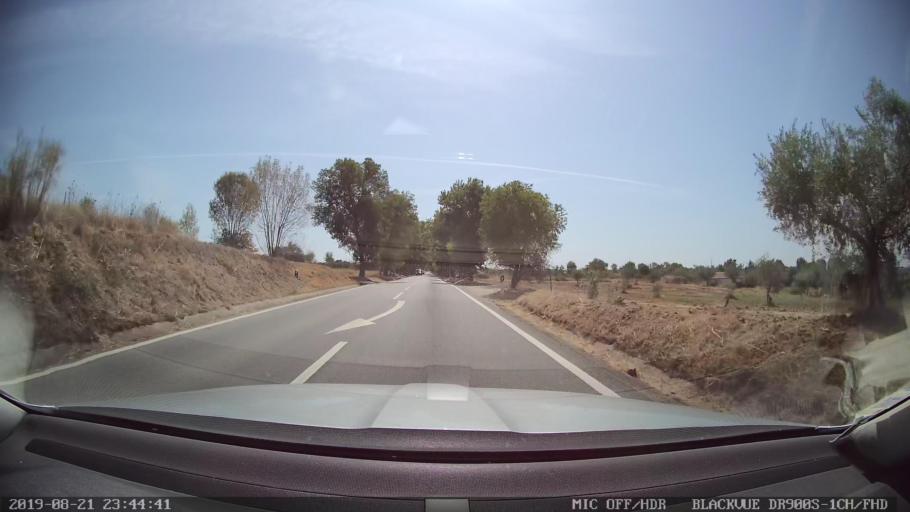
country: PT
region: Castelo Branco
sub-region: Idanha-A-Nova
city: Idanha-a-Nova
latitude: 39.8452
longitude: -7.2749
